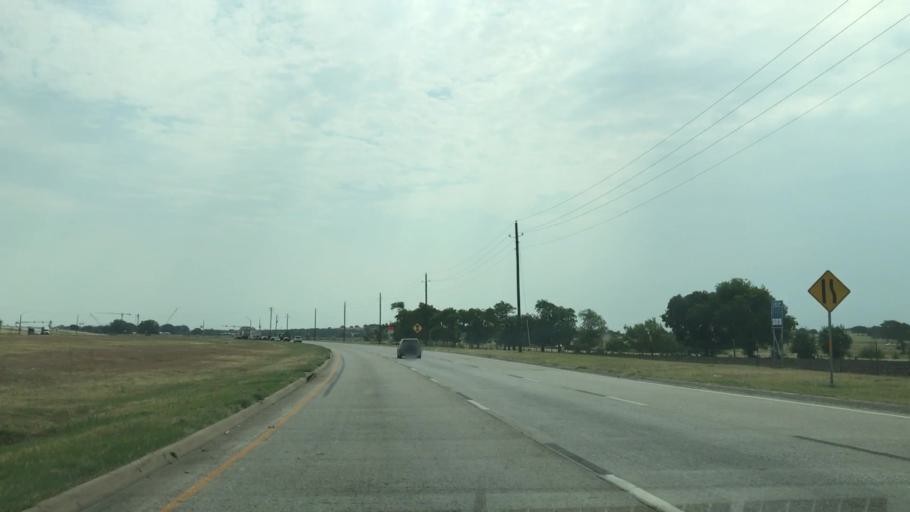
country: US
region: Texas
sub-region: Denton County
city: Roanoke
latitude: 32.9853
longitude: -97.2333
